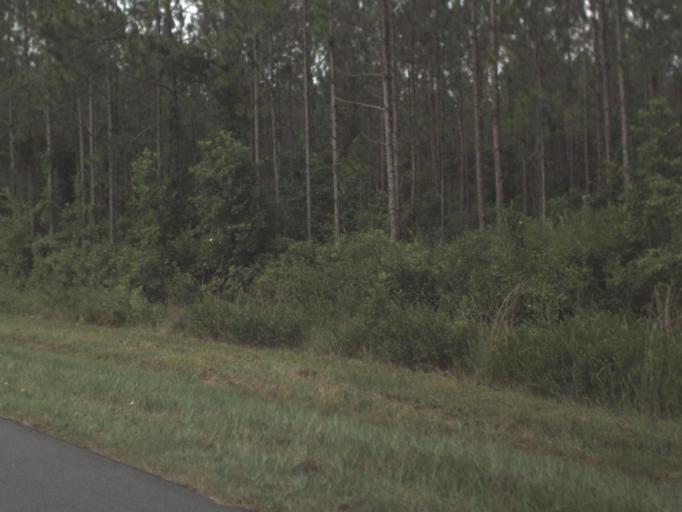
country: US
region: Florida
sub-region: Hamilton County
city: Jasper
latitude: 30.4946
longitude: -82.6636
